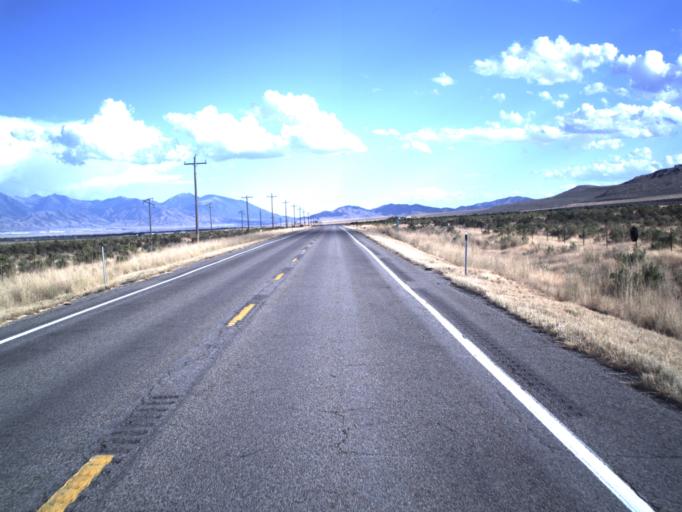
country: US
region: Utah
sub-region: Tooele County
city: Grantsville
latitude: 40.6613
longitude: -112.5399
